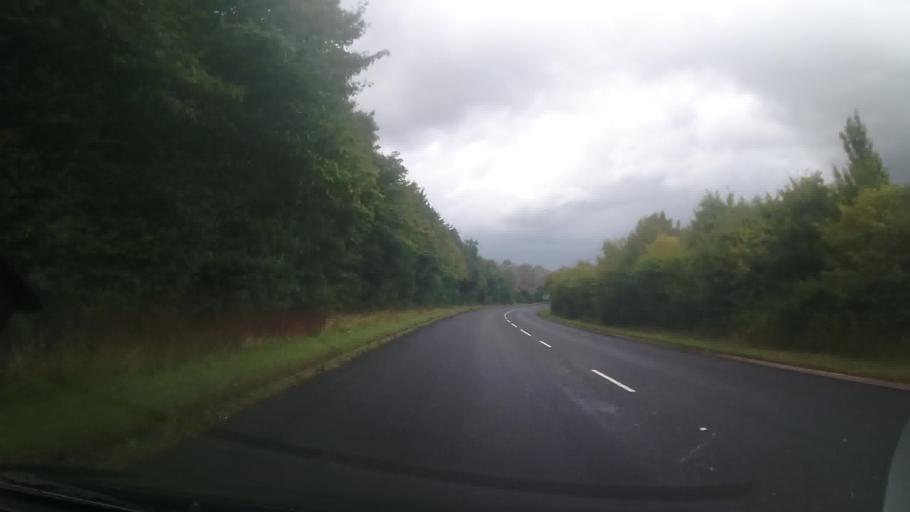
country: GB
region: England
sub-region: Worcestershire
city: Broadway
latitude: 52.0490
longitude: -1.8703
